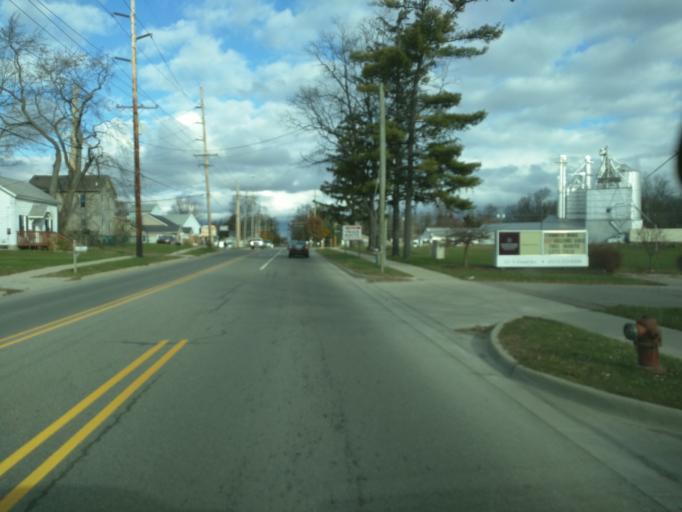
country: US
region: Michigan
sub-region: Livingston County
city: Fowlerville
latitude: 42.6546
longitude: -84.0728
